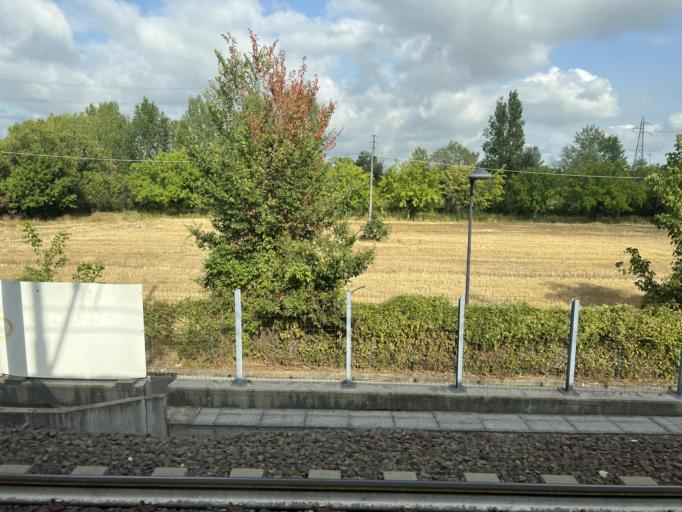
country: IT
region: Emilia-Romagna
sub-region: Provincia di Parma
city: Parma
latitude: 44.8131
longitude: 10.3471
